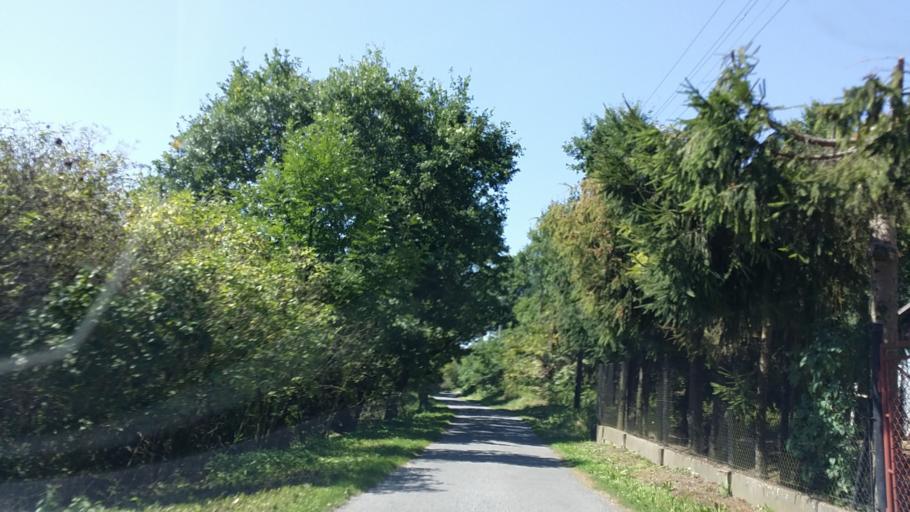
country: PL
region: Lesser Poland Voivodeship
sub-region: Powiat oswiecimski
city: Przeciszow
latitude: 50.0171
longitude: 19.3988
